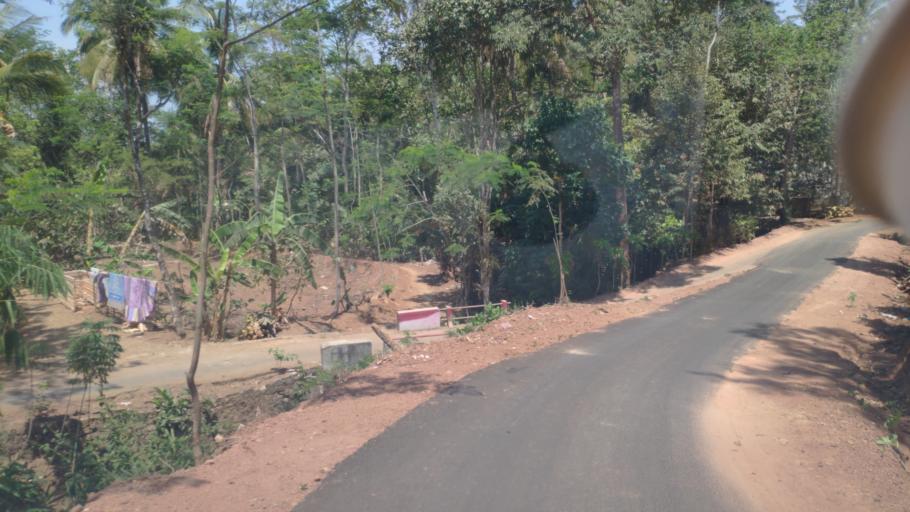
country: ID
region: Central Java
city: Wonosobo
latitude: -7.4246
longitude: 109.6883
